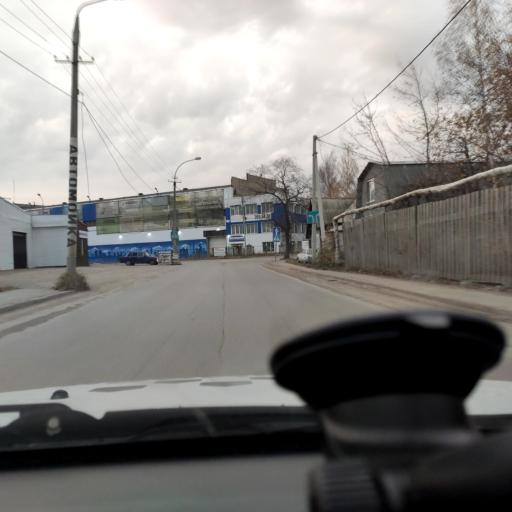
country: RU
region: Perm
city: Perm
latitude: 57.9766
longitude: 56.2671
